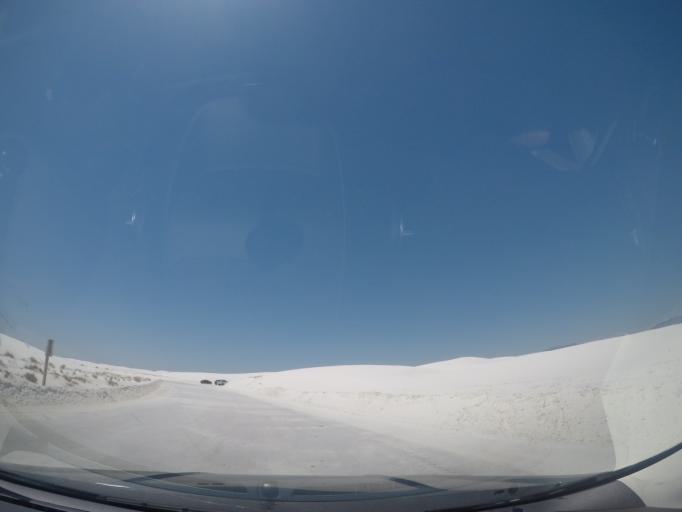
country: US
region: New Mexico
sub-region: Otero County
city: Holloman Air Force Base
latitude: 32.8233
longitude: -106.2720
